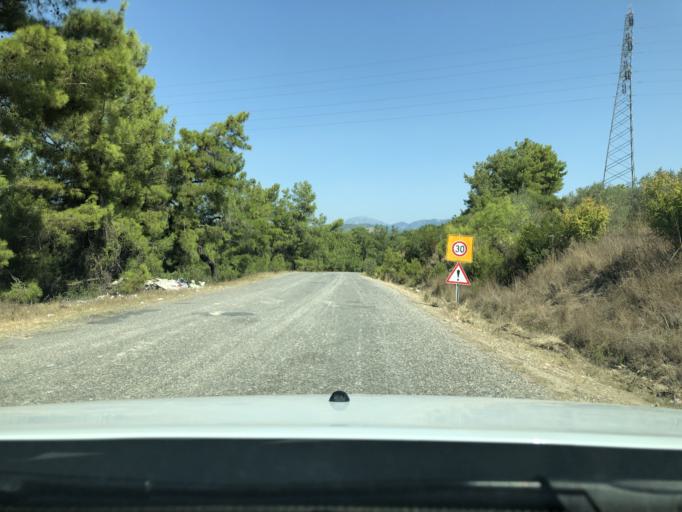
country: TR
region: Antalya
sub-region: Manavgat
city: Manavgat
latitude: 36.8235
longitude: 31.5077
